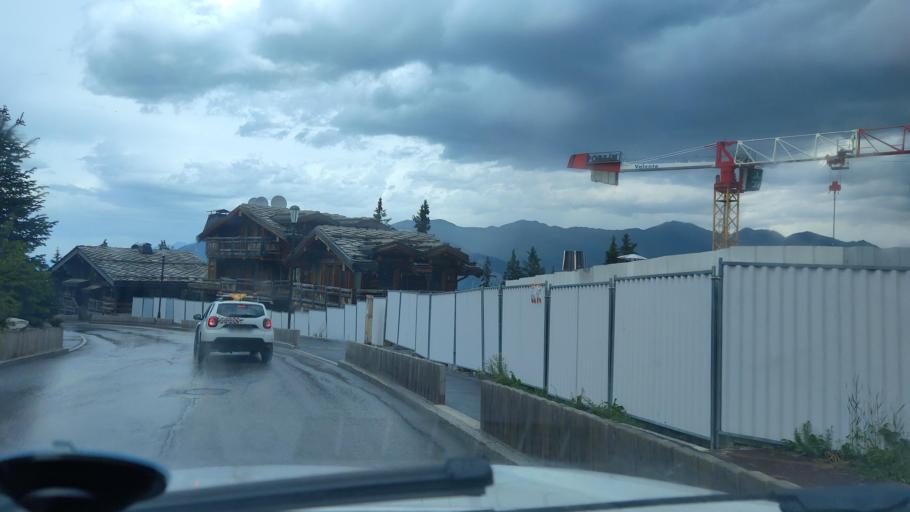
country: FR
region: Rhone-Alpes
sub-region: Departement de la Savoie
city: Courchevel
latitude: 45.4120
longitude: 6.6376
